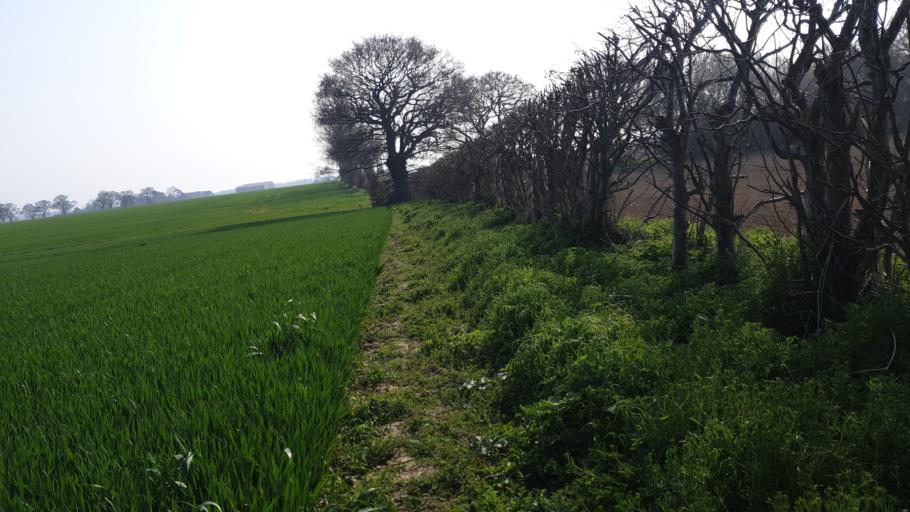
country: GB
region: England
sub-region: Essex
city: Mistley
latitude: 51.8985
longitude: 1.1234
